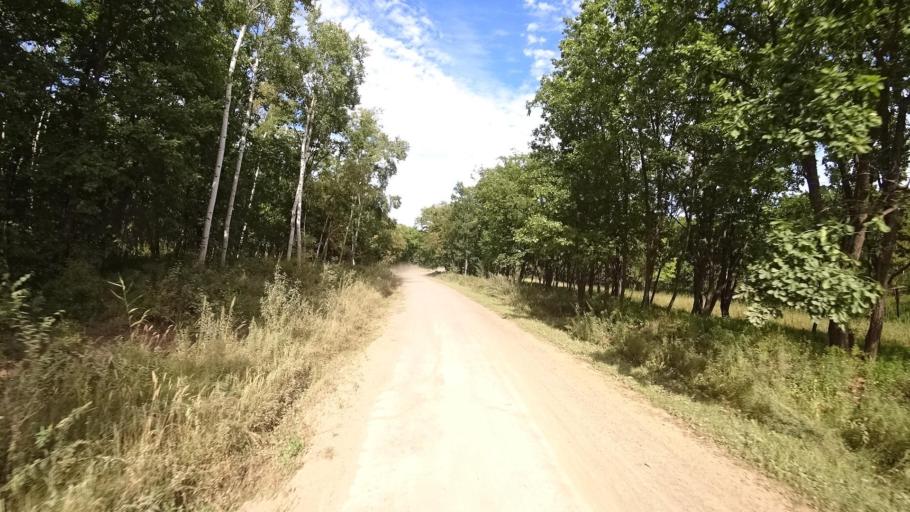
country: RU
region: Primorskiy
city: Yakovlevka
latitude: 44.3924
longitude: 133.5509
